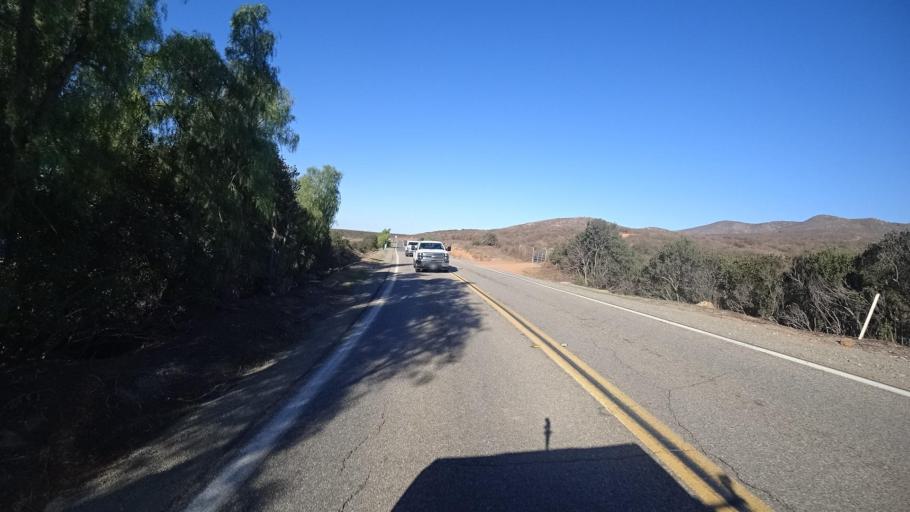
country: US
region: California
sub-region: San Diego County
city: Jamul
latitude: 32.6359
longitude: -116.8905
